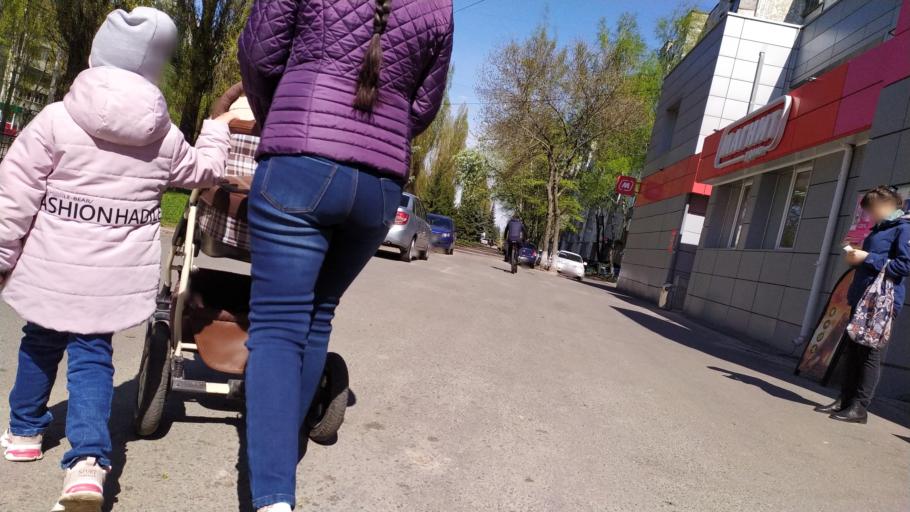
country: RU
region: Kursk
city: Kursk
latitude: 51.7415
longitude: 36.1362
